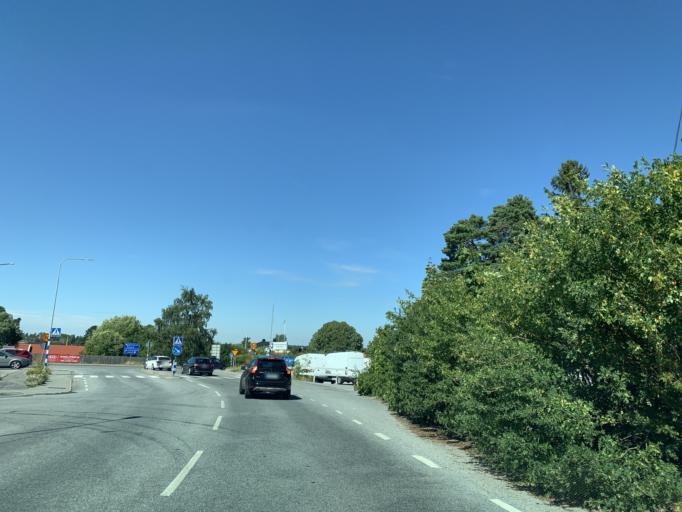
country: SE
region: Stockholm
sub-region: Ekero Kommun
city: Ekeroe
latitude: 59.2755
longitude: 17.7853
